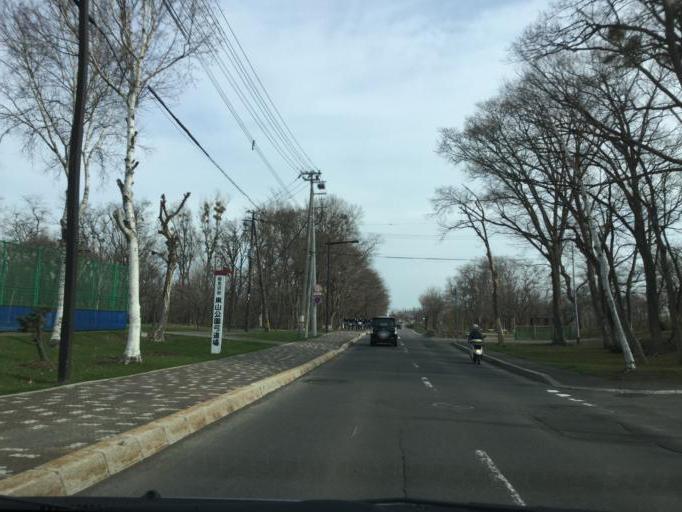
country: JP
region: Hokkaido
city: Iwamizawa
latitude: 43.1908
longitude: 141.7737
